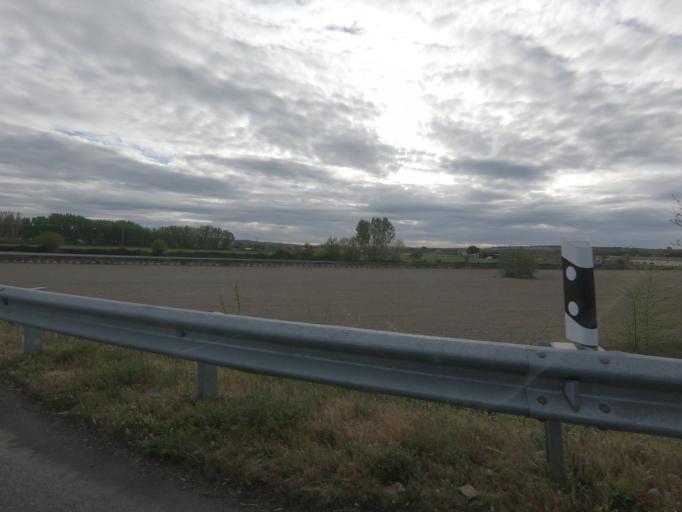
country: ES
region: Extremadura
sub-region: Provincia de Caceres
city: Coria
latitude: 39.9716
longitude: -6.5234
